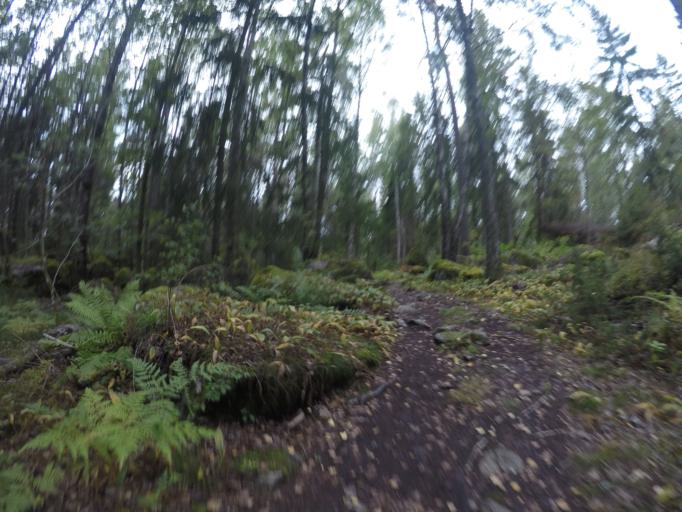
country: SE
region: Vaestmanland
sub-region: Vasteras
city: Vasteras
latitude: 59.6434
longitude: 16.5155
